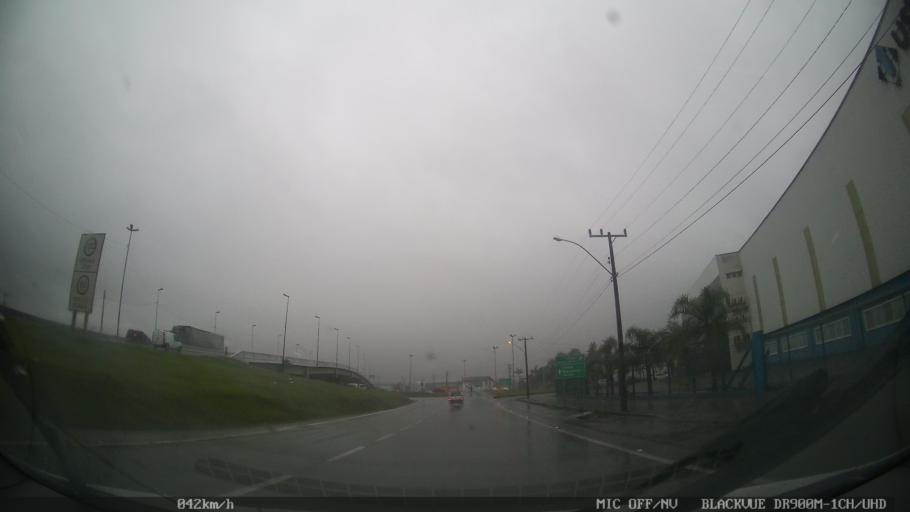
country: BR
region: Santa Catarina
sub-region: Itajai
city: Itajai
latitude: -26.8911
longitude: -48.7206
